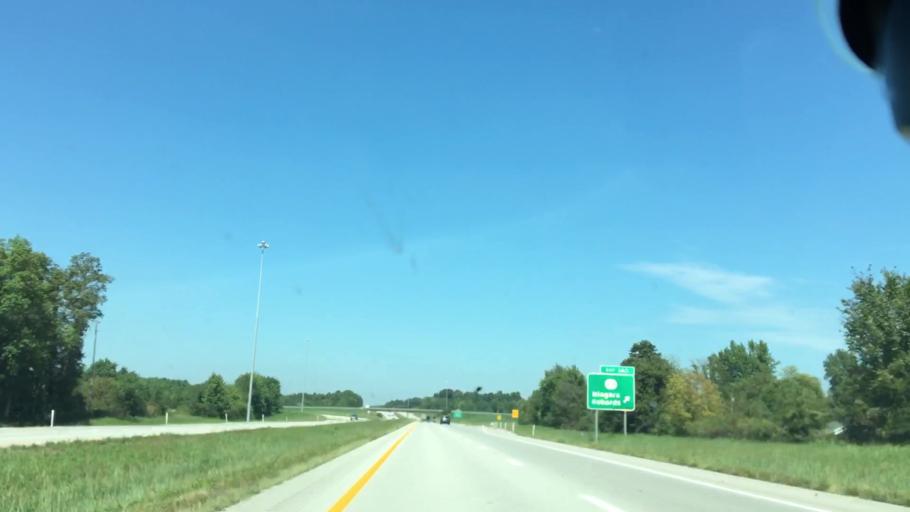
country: US
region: Kentucky
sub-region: Webster County
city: Sebree
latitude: 37.6848
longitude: -87.5136
